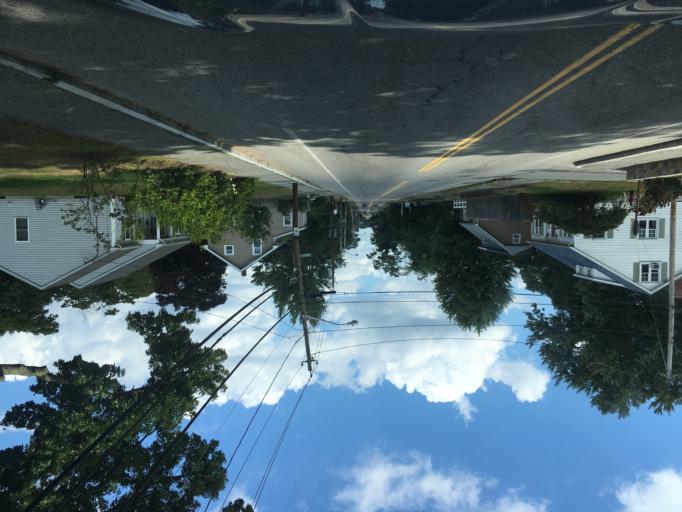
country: US
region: Rhode Island
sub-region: Kent County
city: Warwick
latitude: 41.6953
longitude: -71.3985
